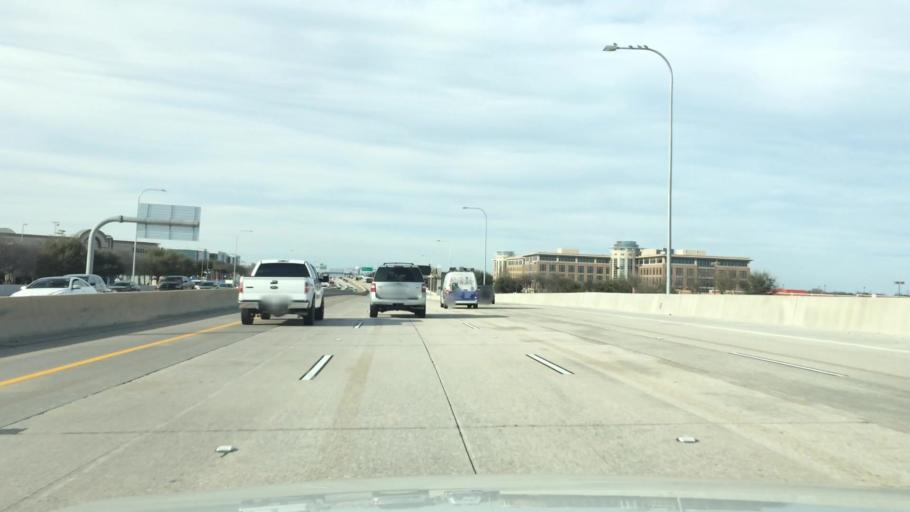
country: US
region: Texas
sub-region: Dallas County
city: Addison
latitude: 33.0284
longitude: -96.8292
